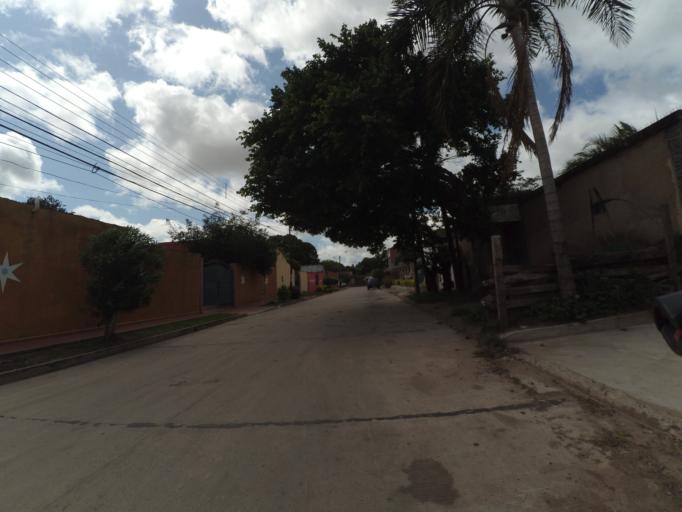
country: BO
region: Santa Cruz
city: Santa Cruz de la Sierra
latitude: -17.7971
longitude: -63.2192
